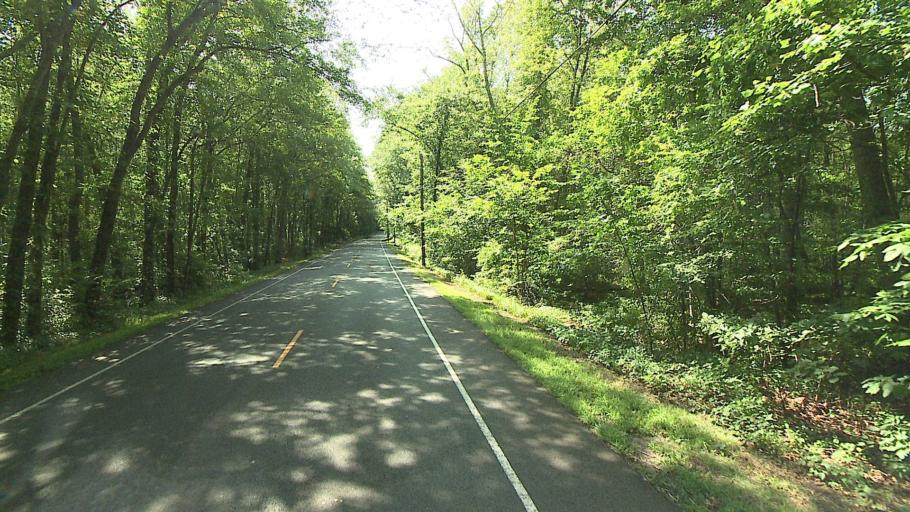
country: US
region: Connecticut
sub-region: Fairfield County
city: Trumbull
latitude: 41.2801
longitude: -73.2947
